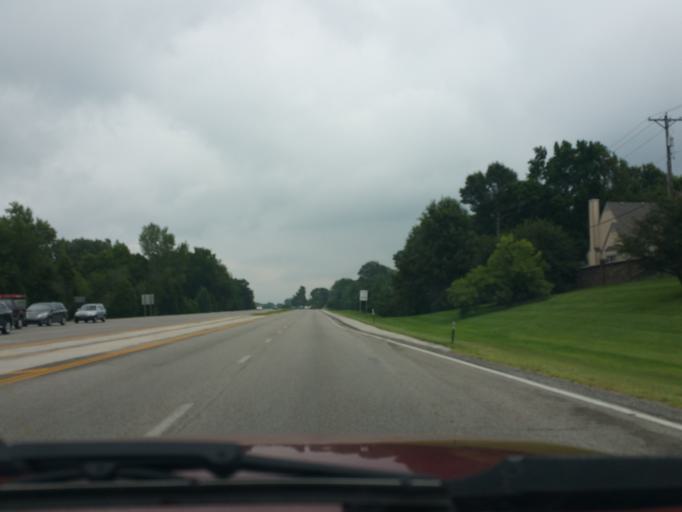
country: US
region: Kansas
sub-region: Johnson County
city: Mission
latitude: 39.0149
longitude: -94.6582
